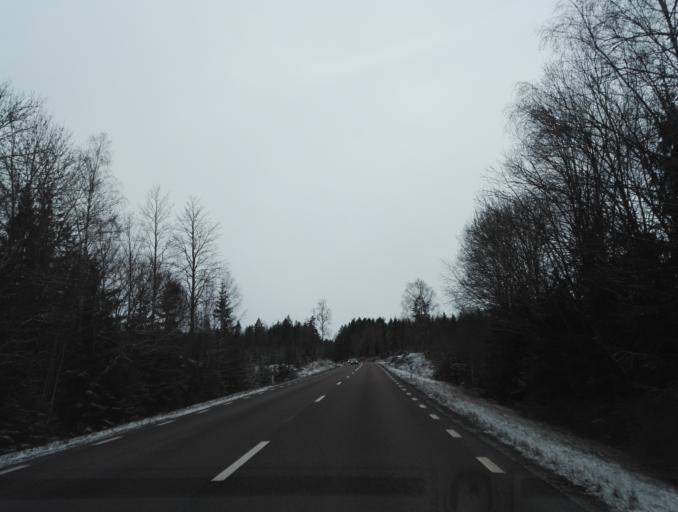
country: SE
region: Kalmar
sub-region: Hultsfreds Kommun
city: Virserum
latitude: 57.2051
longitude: 15.5190
